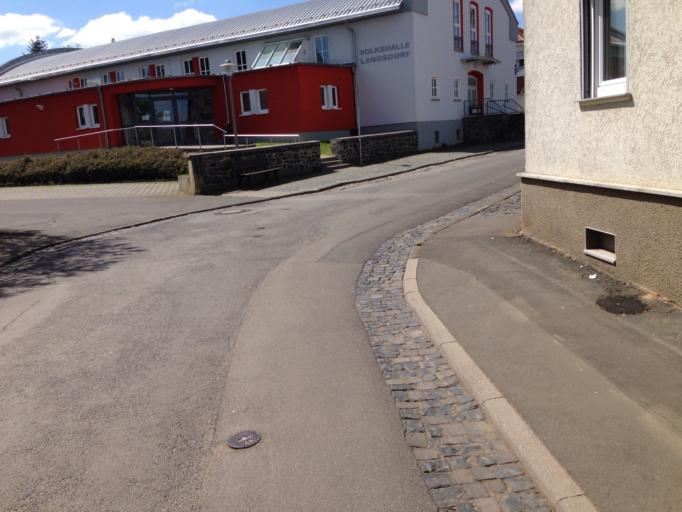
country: DE
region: Hesse
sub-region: Regierungsbezirk Giessen
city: Hungen
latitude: 50.4940
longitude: 8.8530
